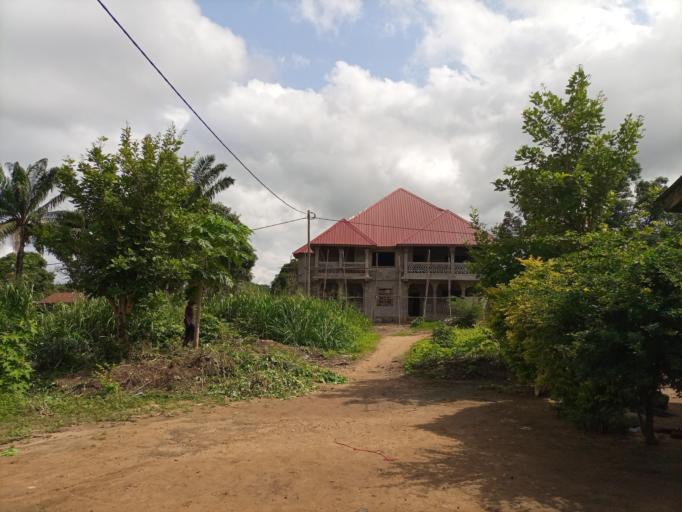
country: SL
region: Southern Province
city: Bo
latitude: 7.9606
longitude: -11.7611
